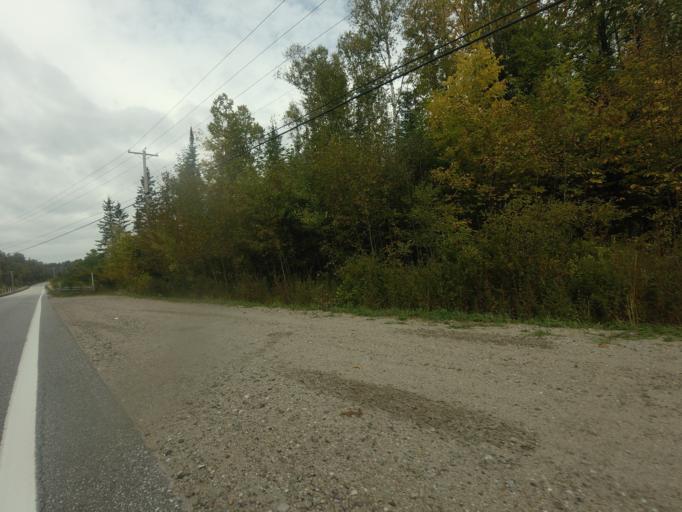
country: CA
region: Quebec
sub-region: Outaouais
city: Wakefield
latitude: 45.9324
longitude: -75.9866
